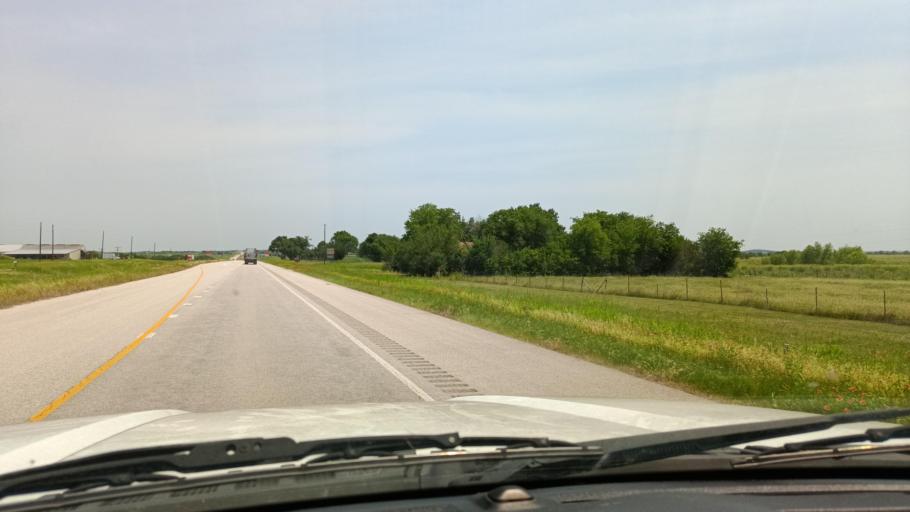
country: US
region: Texas
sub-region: Bell County
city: Little River-Academy
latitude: 30.9969
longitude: -97.2875
